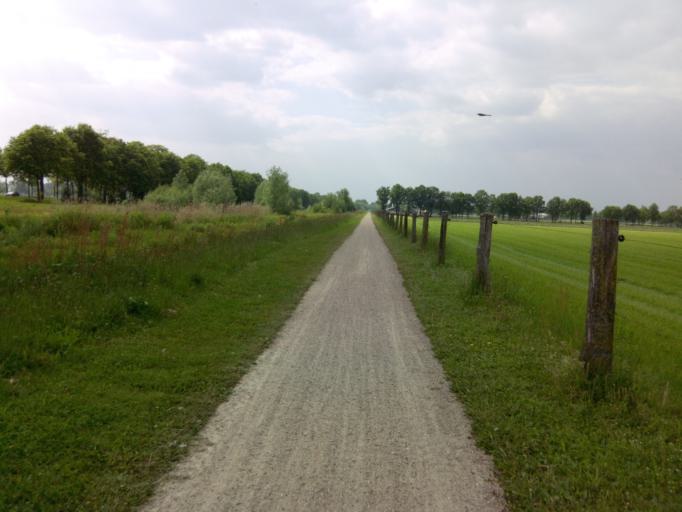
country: NL
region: Gelderland
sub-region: Oost Gelre
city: Lichtenvoorde
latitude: 52.0470
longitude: 6.5444
